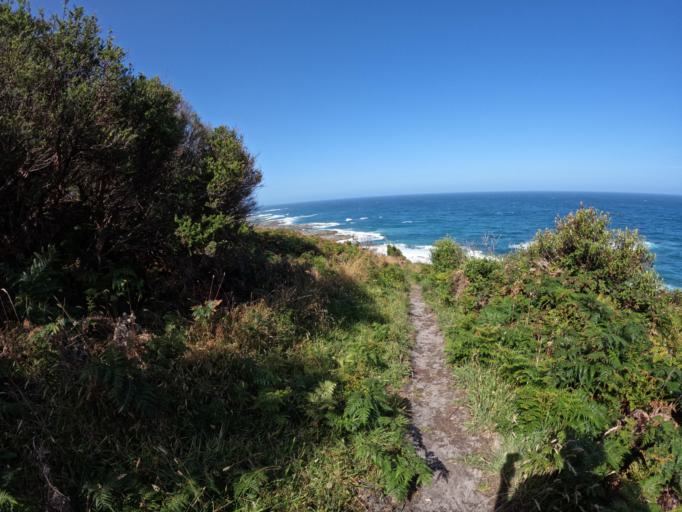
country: AU
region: Victoria
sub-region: Colac-Otway
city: Apollo Bay
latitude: -38.7900
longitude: 143.6470
